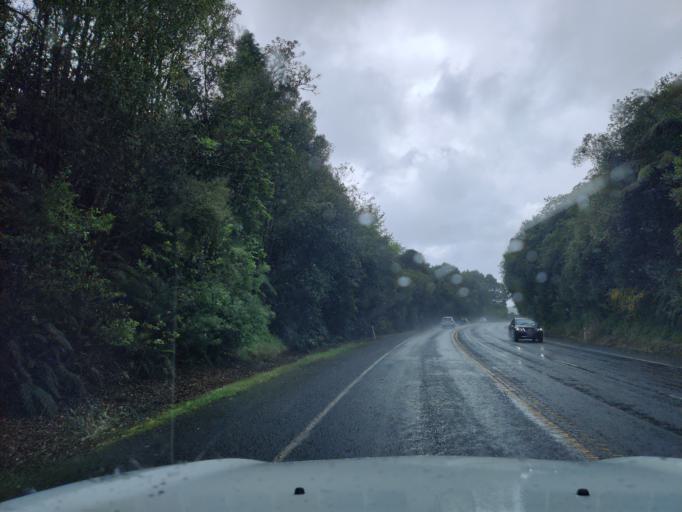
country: NZ
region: Bay of Plenty
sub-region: Rotorua District
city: Rotorua
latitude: -38.0726
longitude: 176.1701
